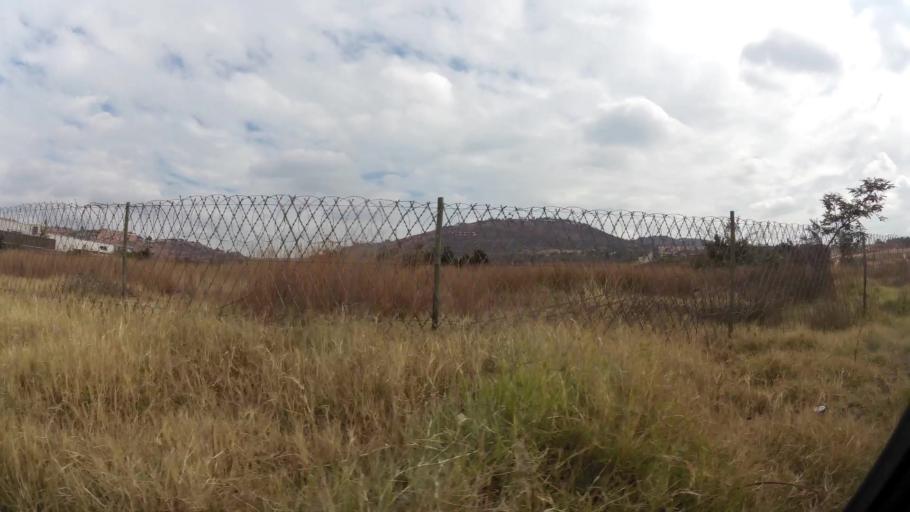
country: ZA
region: Gauteng
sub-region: City of Johannesburg Metropolitan Municipality
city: Roodepoort
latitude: -26.1072
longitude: 27.8861
